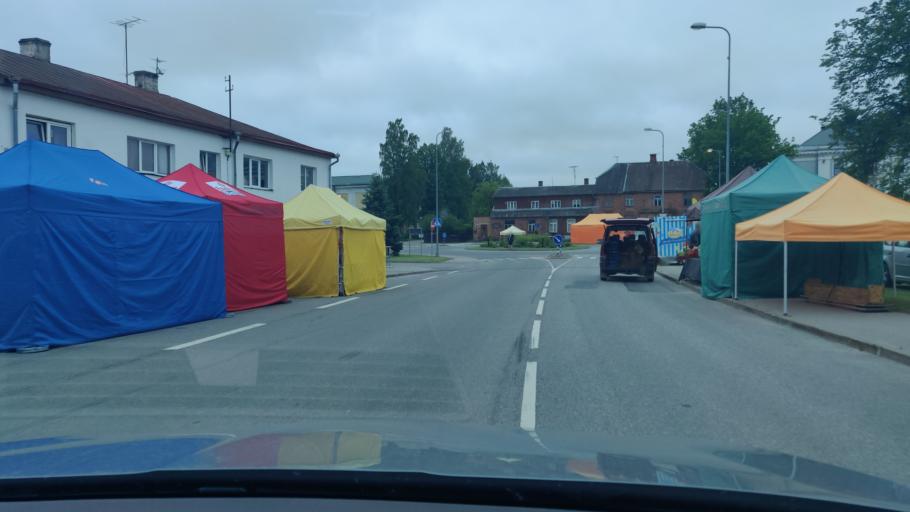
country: EE
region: Vorumaa
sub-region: Voru linn
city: Voru
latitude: 57.7327
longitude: 27.2834
